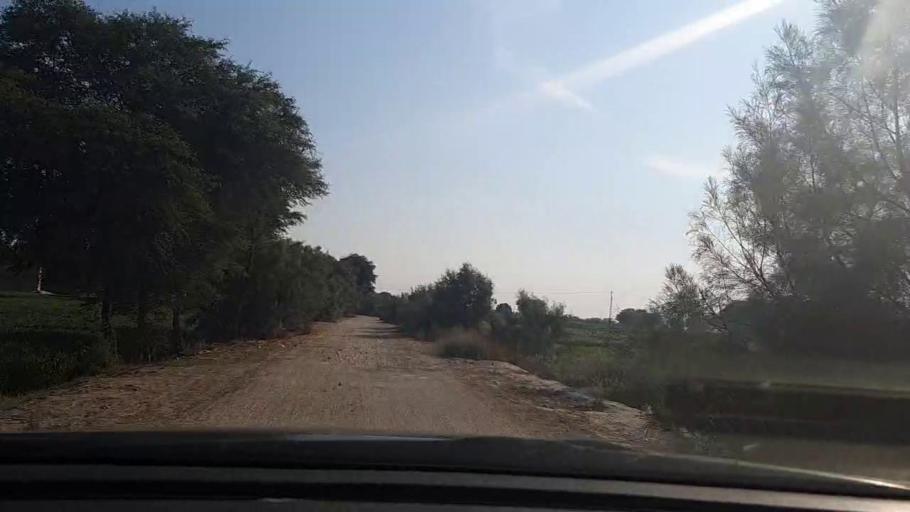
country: PK
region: Sindh
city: Sehwan
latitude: 26.3077
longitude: 68.0011
